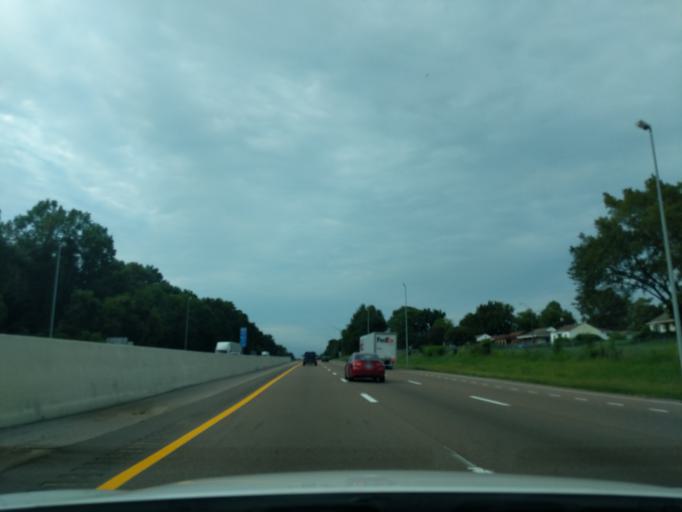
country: US
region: Tennessee
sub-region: Shelby County
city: New South Memphis
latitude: 35.0909
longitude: -90.0766
